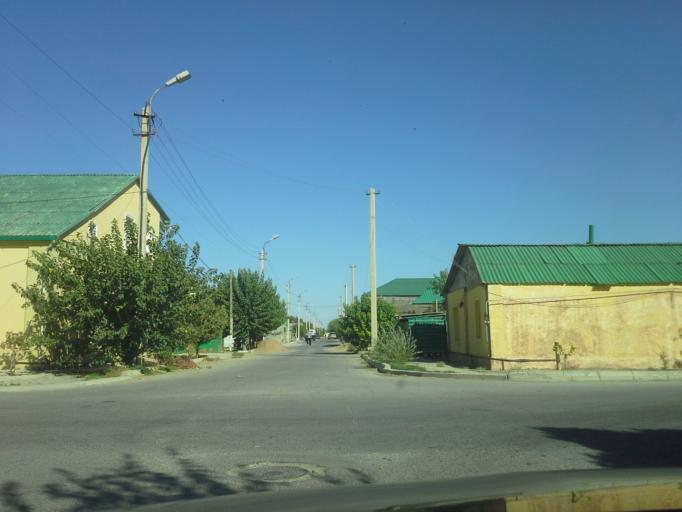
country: TM
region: Ahal
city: Abadan
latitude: 38.0725
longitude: 58.1516
